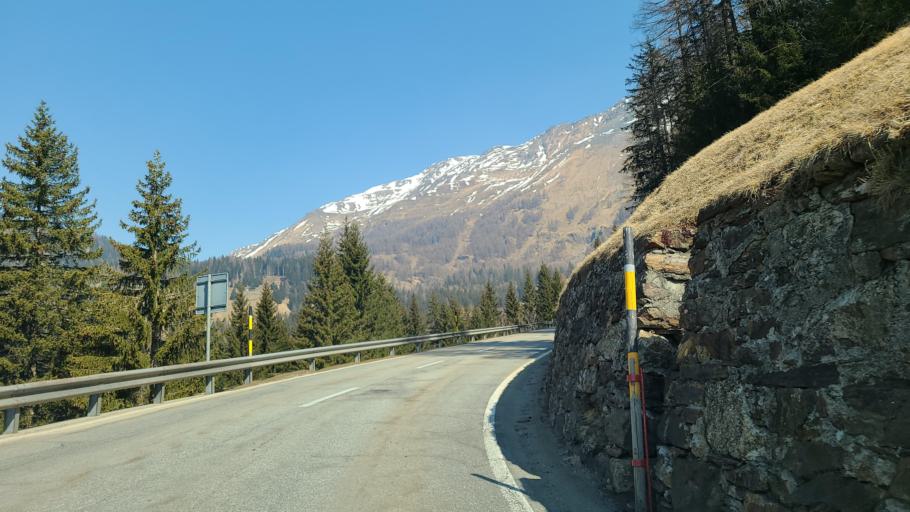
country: CH
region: Grisons
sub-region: Bernina District
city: Poschiavo
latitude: 46.3826
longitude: 10.0739
